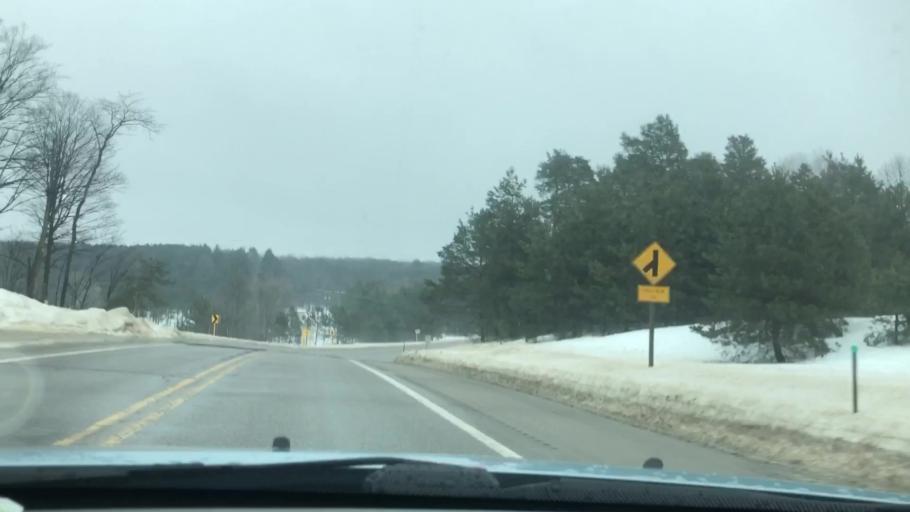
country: US
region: Michigan
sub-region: Otsego County
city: Gaylord
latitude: 45.0612
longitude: -84.7801
